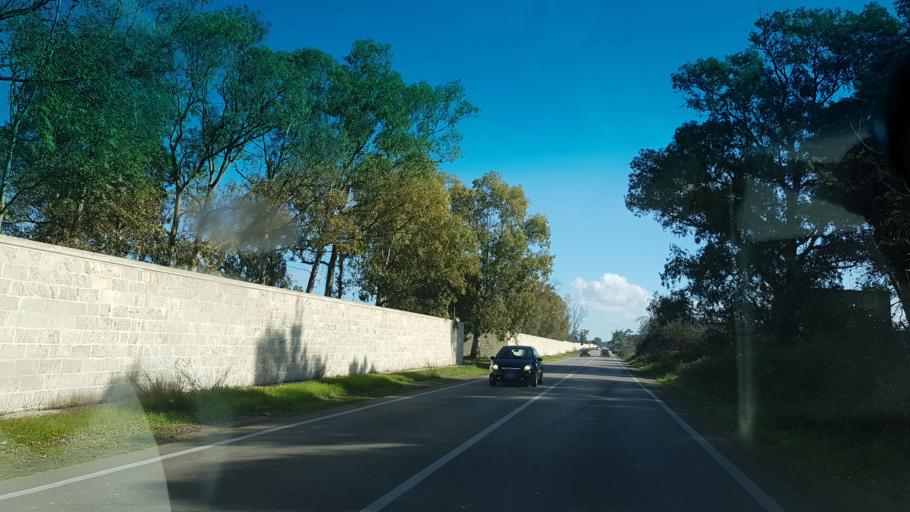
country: IT
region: Apulia
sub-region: Provincia di Lecce
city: Arnesano
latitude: 40.3590
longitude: 18.1124
